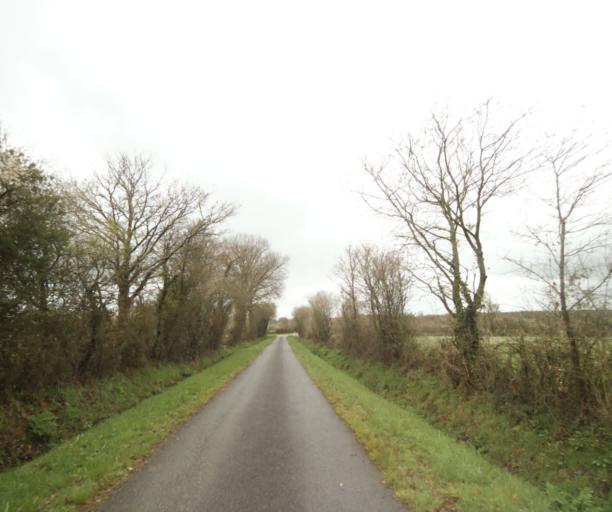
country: FR
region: Pays de la Loire
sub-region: Departement de la Loire-Atlantique
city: Quilly
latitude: 47.4588
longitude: -1.9013
